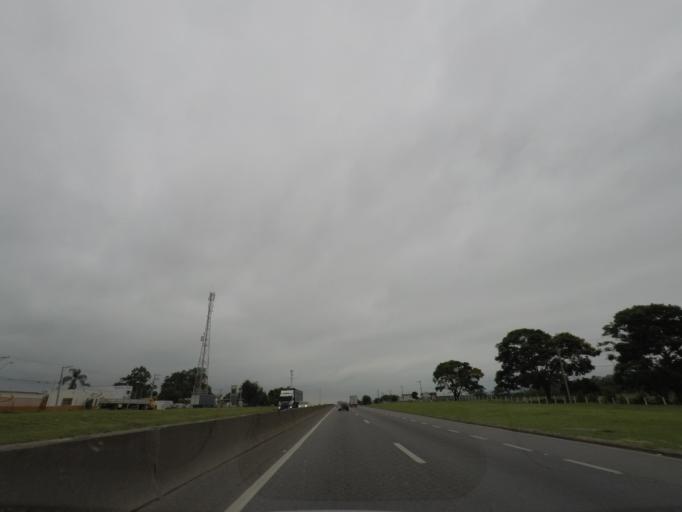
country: BR
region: Sao Paulo
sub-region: Pindamonhangaba
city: Pindamonhangaba
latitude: -22.9538
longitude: -45.4077
